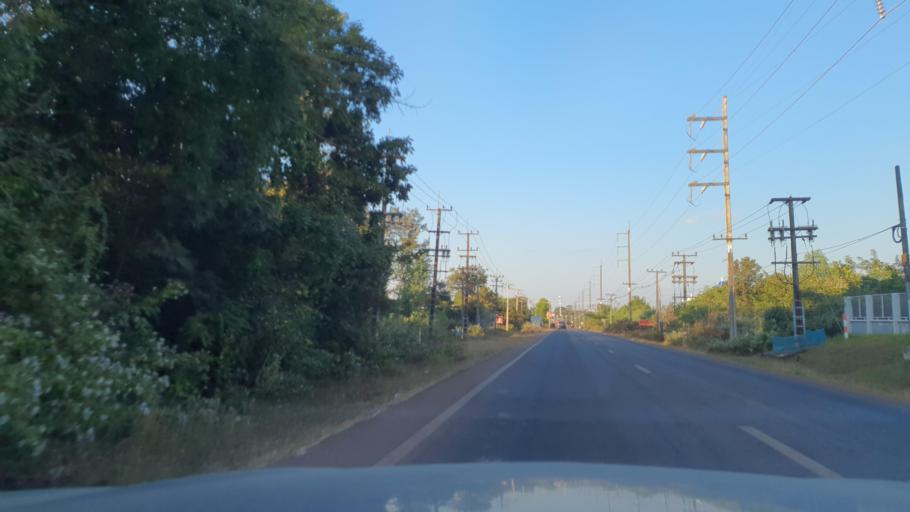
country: TH
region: Nakhon Phanom
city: Si Songkhram
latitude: 17.5796
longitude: 104.2328
